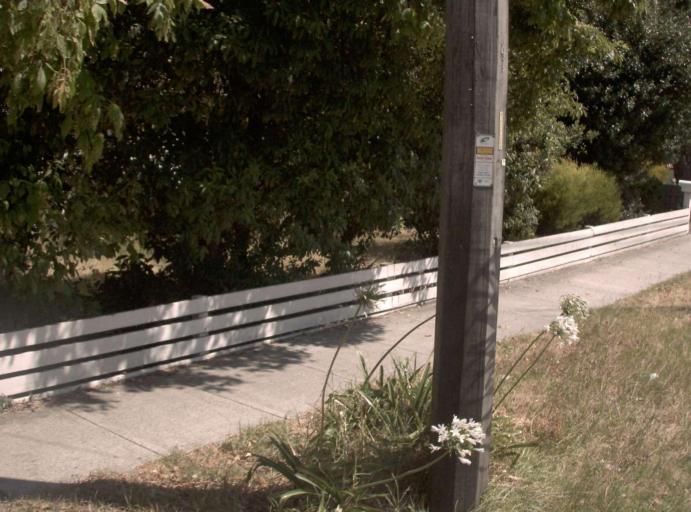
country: AU
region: Victoria
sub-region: Monash
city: Oakleigh South
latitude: -37.9260
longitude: 145.0820
